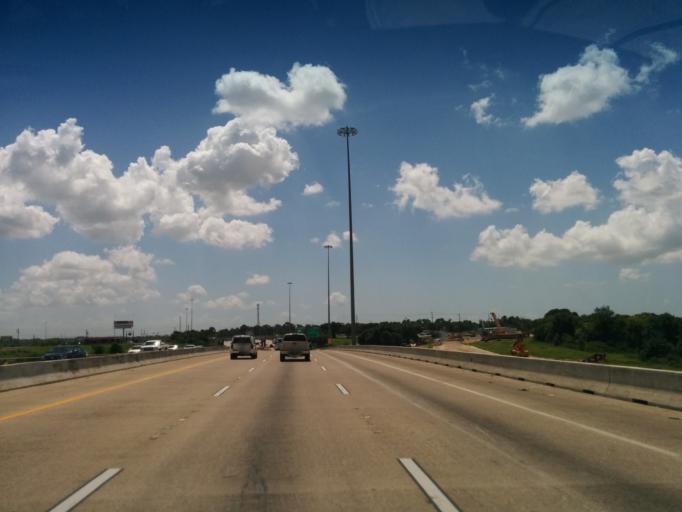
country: US
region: Texas
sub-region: Harris County
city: Highlands
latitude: 29.7926
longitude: -95.0615
